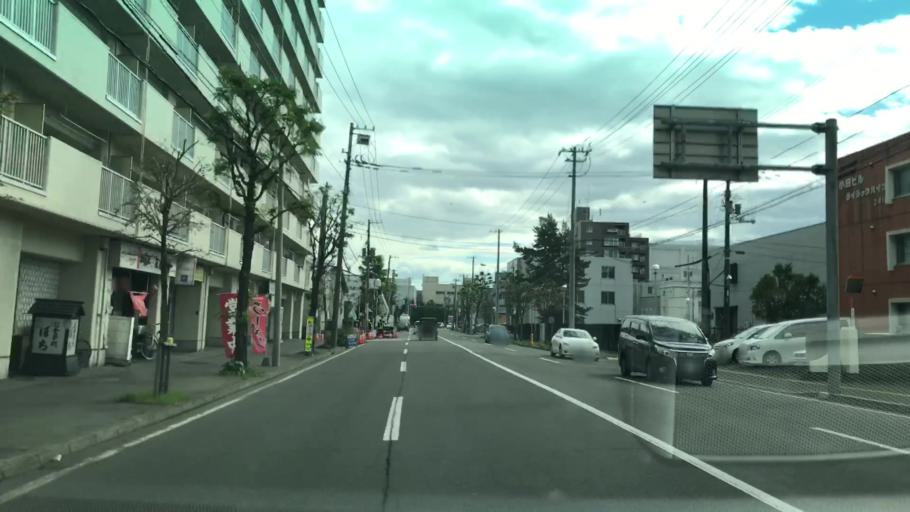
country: JP
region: Hokkaido
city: Sapporo
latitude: 43.0751
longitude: 141.3147
